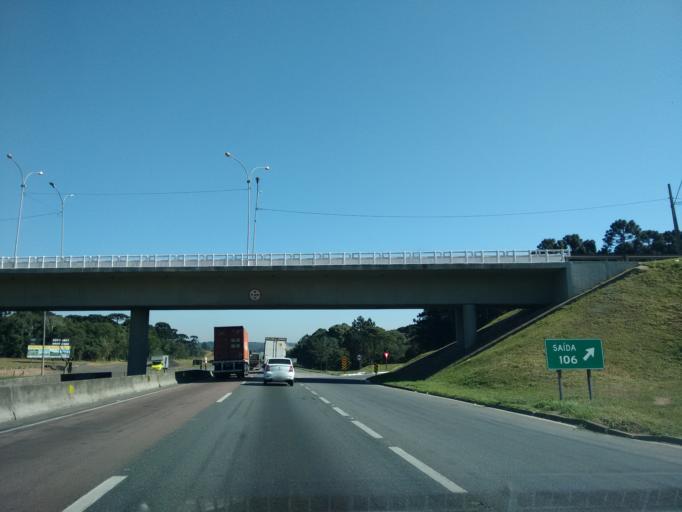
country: BR
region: Parana
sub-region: Sao Jose Dos Pinhais
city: Sao Jose dos Pinhais
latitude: -25.5700
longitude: -49.2189
